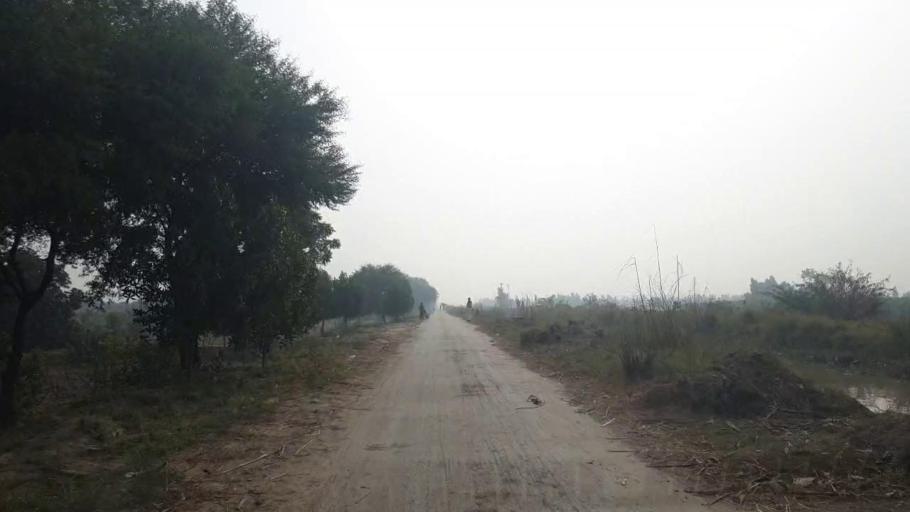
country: PK
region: Sindh
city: Tando Adam
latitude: 25.7655
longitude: 68.6078
